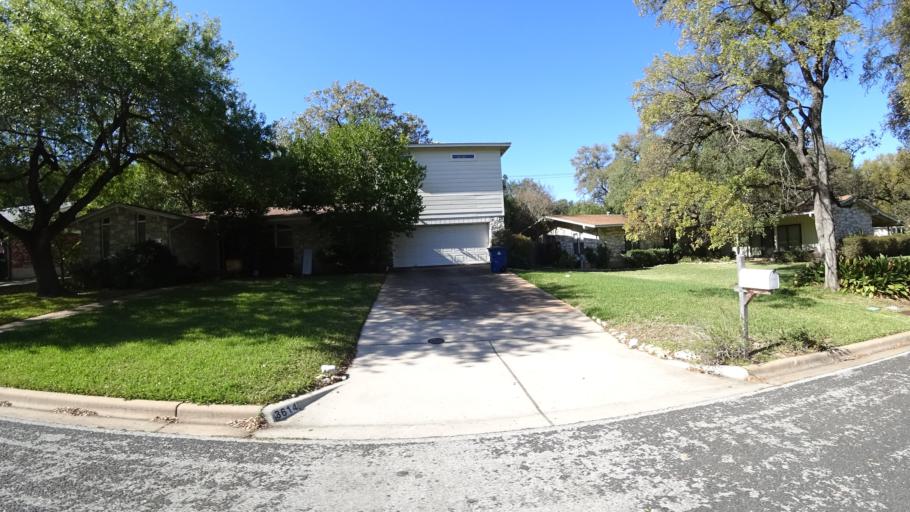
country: US
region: Texas
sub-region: Williamson County
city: Jollyville
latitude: 30.3766
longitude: -97.7443
